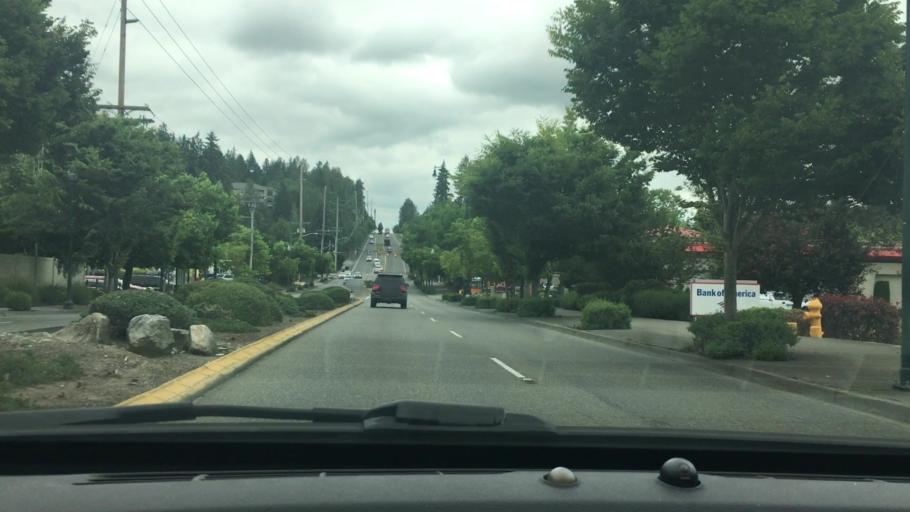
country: US
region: Washington
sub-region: King County
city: City of Sammamish
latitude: 47.6143
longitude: -122.0354
